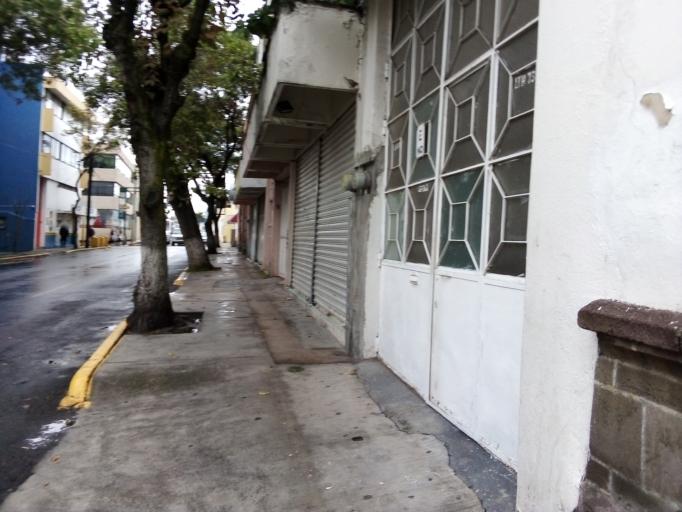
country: MX
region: Mexico
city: Toluca
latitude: 19.2868
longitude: -99.6577
